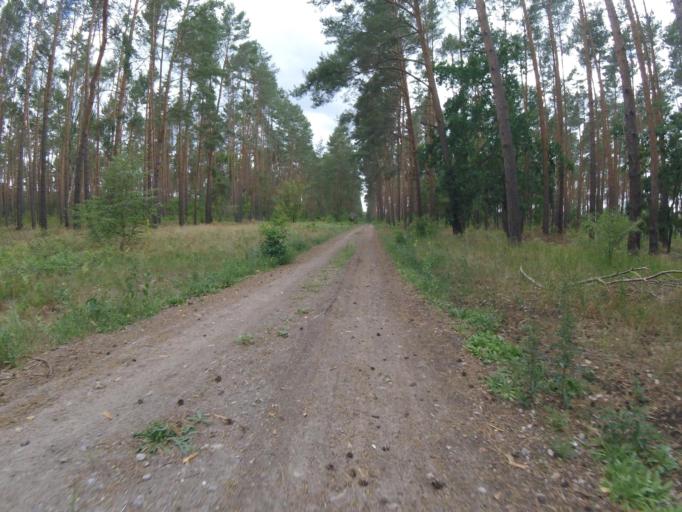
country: DE
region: Brandenburg
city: Wildau
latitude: 52.3197
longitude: 13.6818
